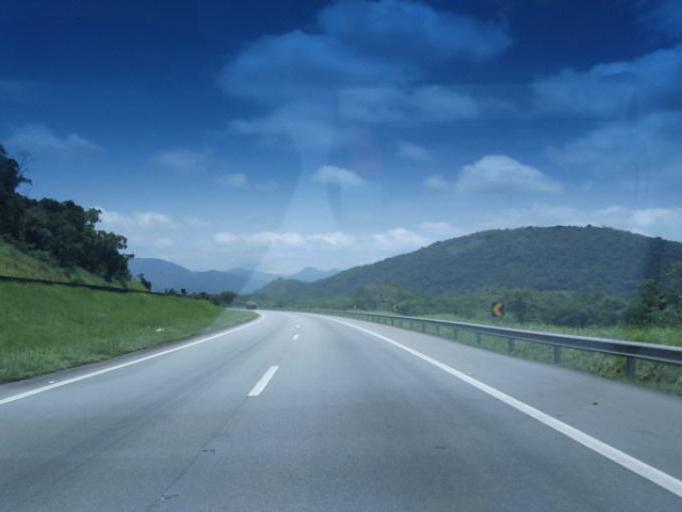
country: BR
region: Sao Paulo
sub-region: Miracatu
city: Miracatu
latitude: -24.2038
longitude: -47.3722
